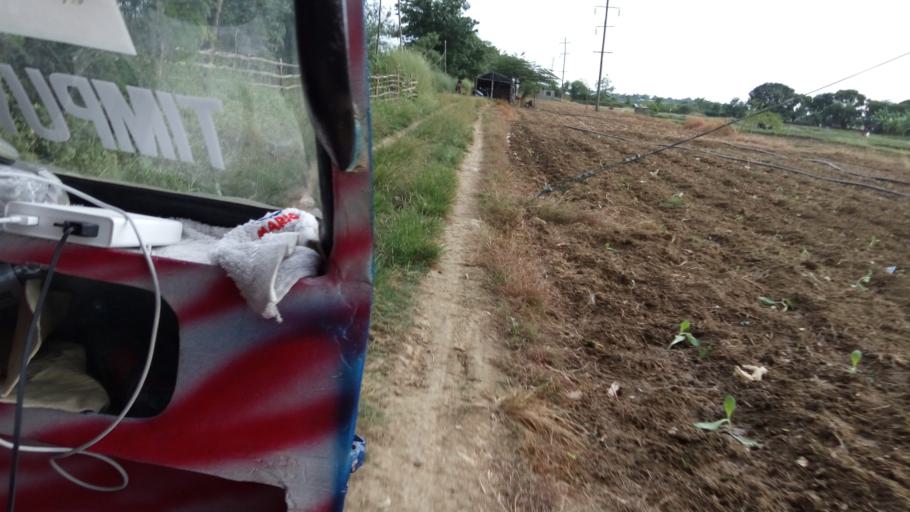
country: PH
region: Ilocos
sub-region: Province of La Union
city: Santo Tomas
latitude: 16.2760
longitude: 120.3881
